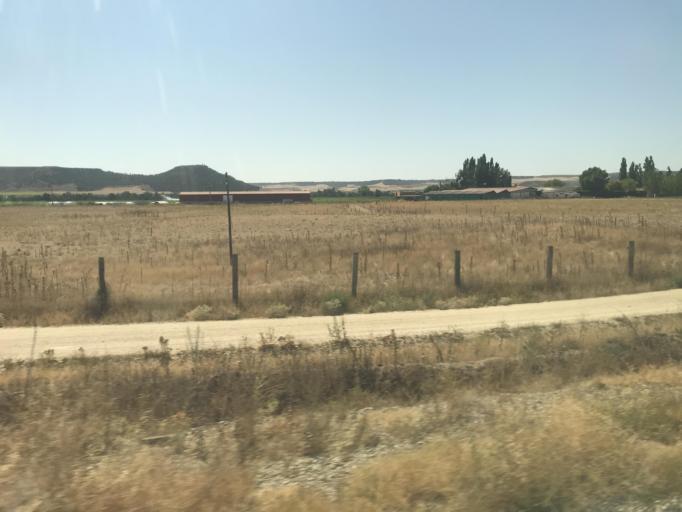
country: ES
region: Castille and Leon
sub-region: Provincia de Valladolid
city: Cubillas de Santa Marta
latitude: 41.7993
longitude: -4.5872
